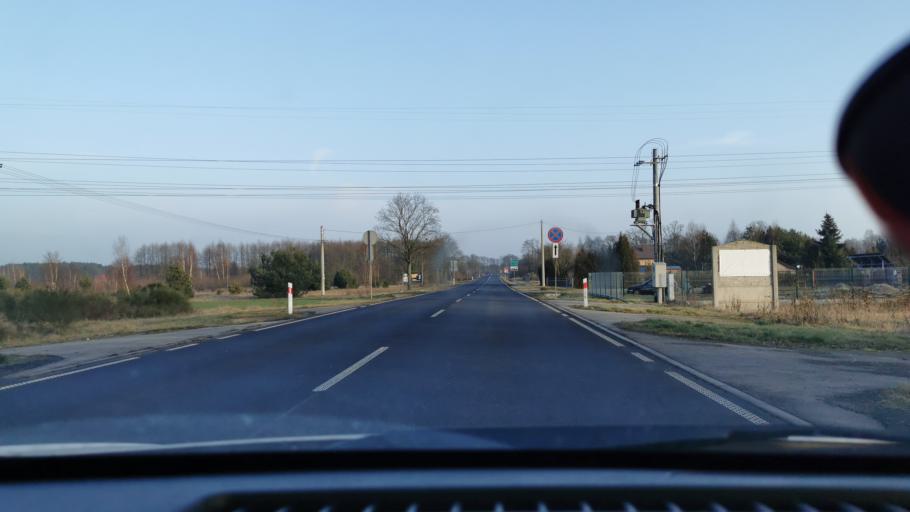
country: PL
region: Lodz Voivodeship
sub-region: Powiat belchatowski
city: Zelow
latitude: 51.5270
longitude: 19.2938
